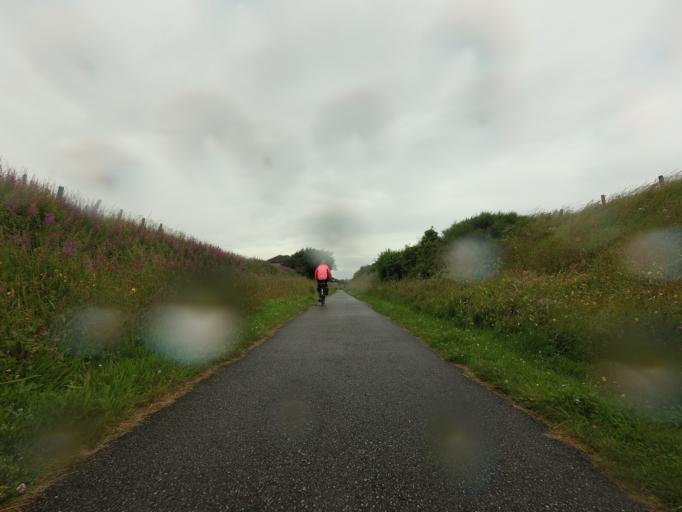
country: GB
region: Scotland
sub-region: Moray
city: Buckie
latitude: 57.6831
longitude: -2.9382
